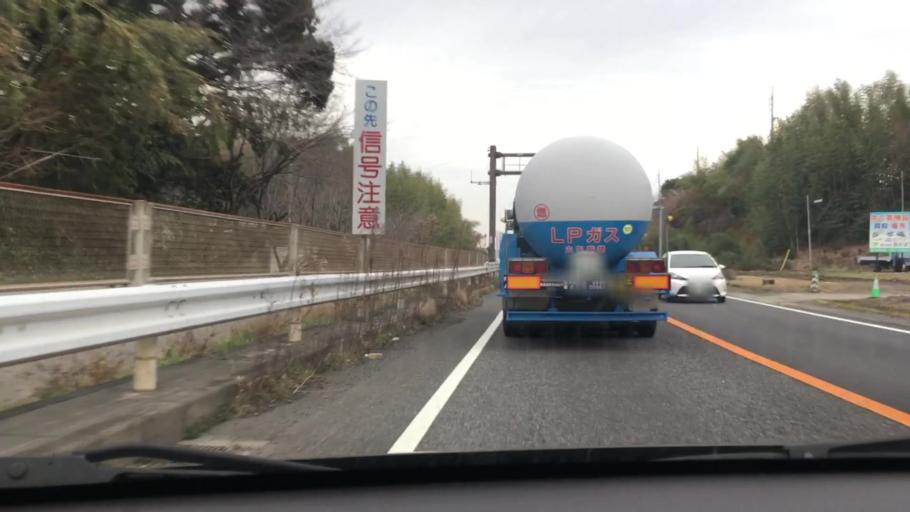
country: JP
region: Mie
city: Kameyama
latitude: 34.8624
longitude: 136.4818
